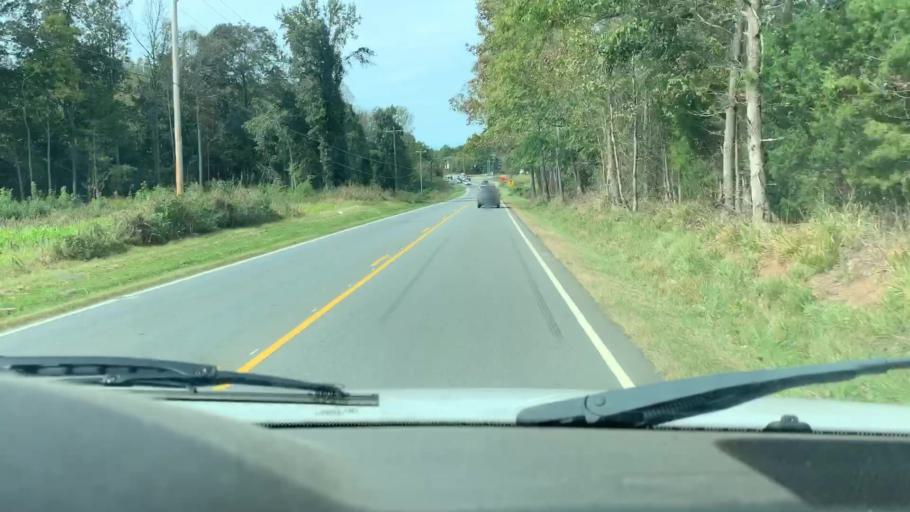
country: US
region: North Carolina
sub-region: Mecklenburg County
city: Huntersville
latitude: 35.4528
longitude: -80.7993
